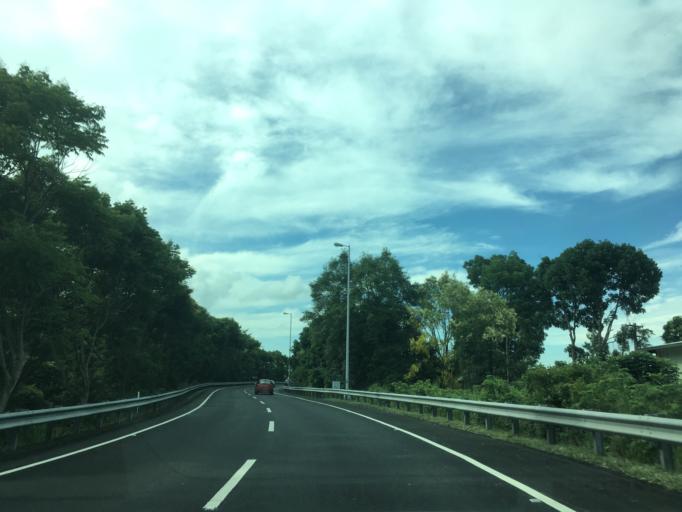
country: TW
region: Taiwan
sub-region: Chiayi
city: Jiayi Shi
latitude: 23.4512
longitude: 120.4870
